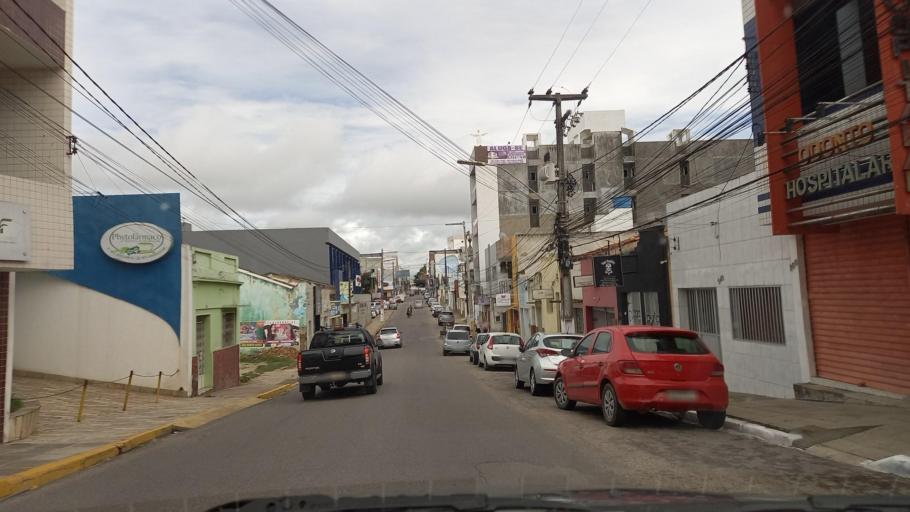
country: BR
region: Pernambuco
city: Garanhuns
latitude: -8.8872
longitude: -36.4884
